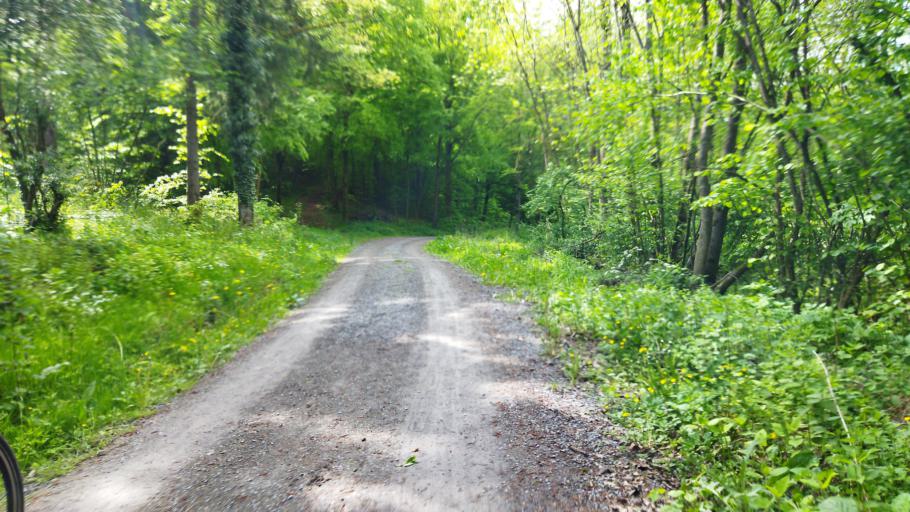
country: DE
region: Baden-Wuerttemberg
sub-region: Regierungsbezirk Stuttgart
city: Bad Rappenau
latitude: 49.2056
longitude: 9.1203
